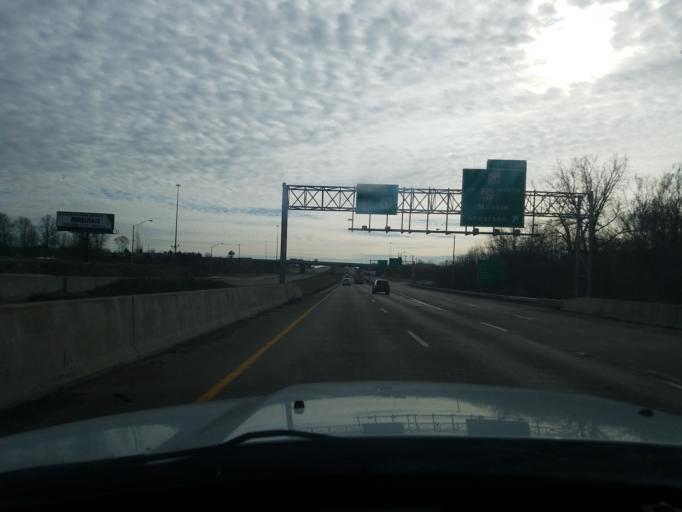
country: US
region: Indiana
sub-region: Delaware County
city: Daleville
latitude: 40.1213
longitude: -85.5689
